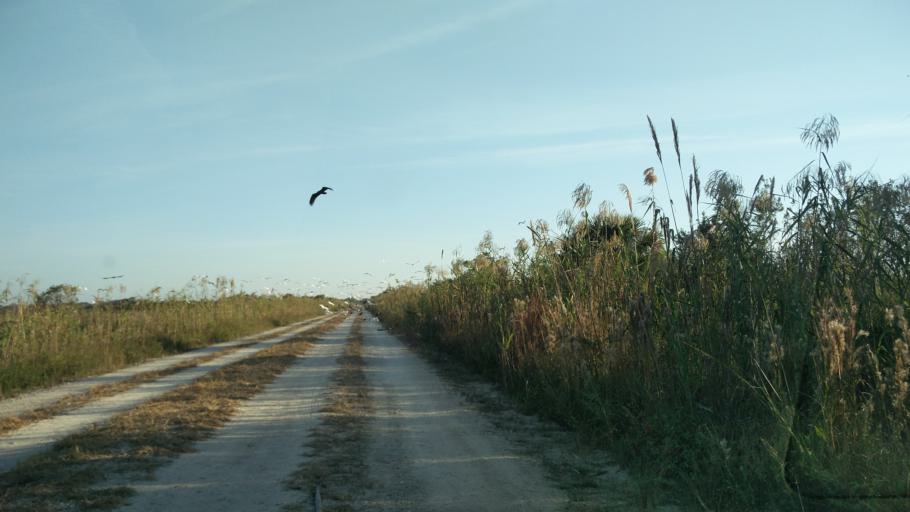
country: US
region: Florida
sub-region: Collier County
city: Lely Resort
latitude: 25.9696
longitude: -81.3673
